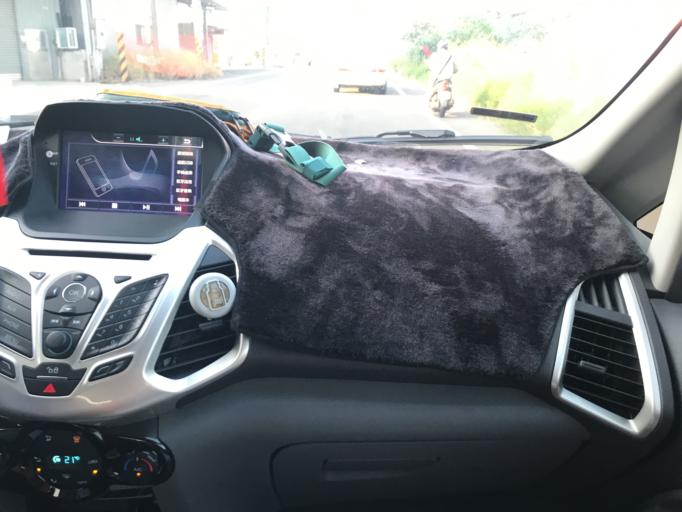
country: TW
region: Taiwan
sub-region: Hsinchu
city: Zhubei
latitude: 24.8350
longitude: 121.0363
